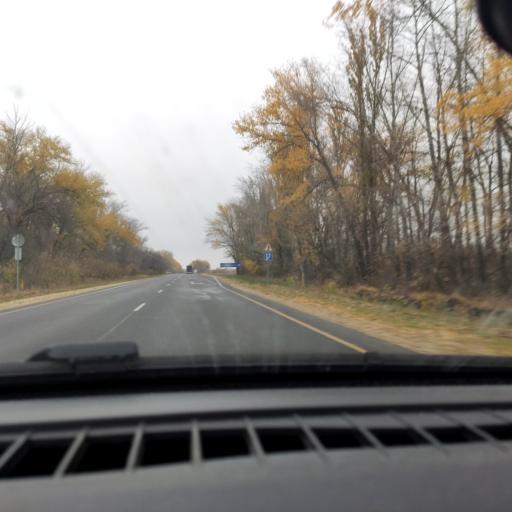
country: RU
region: Voronezj
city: Uryv-Pokrovka
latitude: 51.1678
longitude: 39.0731
